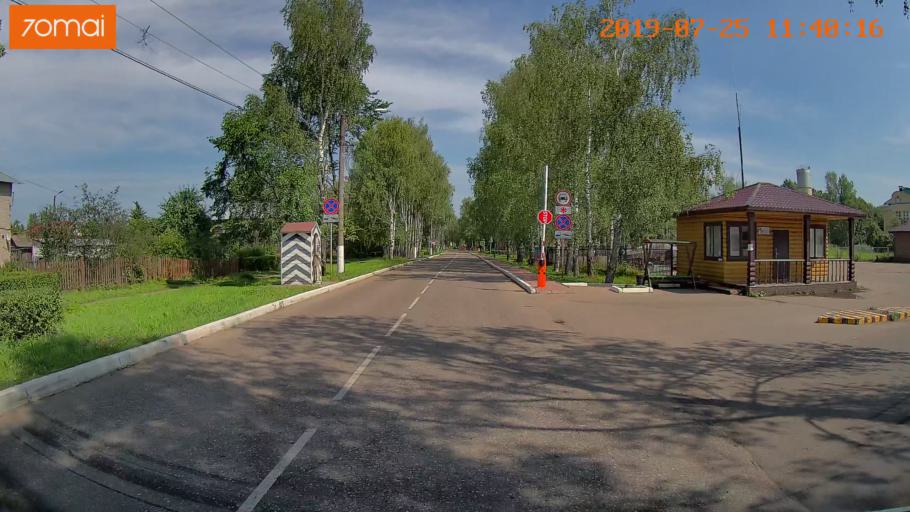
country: RU
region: Ivanovo
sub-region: Privolzhskiy Rayon
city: Ples
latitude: 57.4526
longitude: 41.5056
